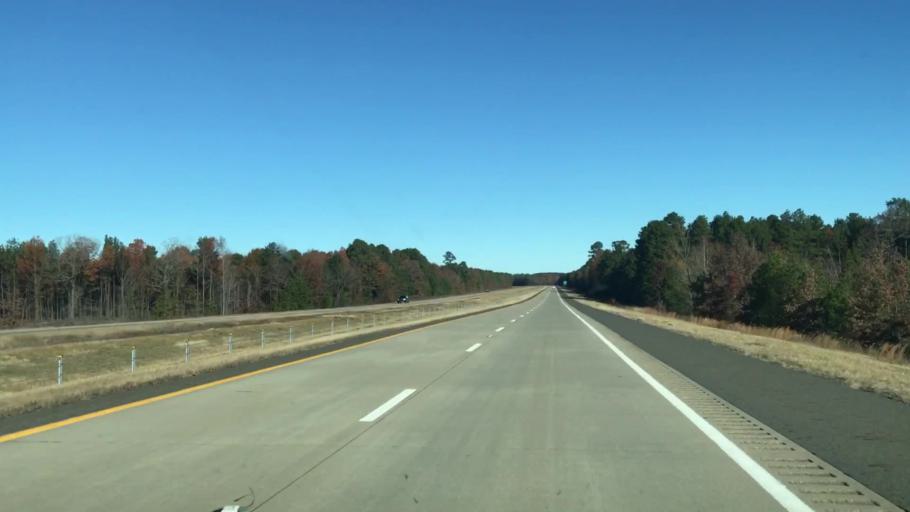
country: US
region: Texas
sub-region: Bowie County
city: Texarkana
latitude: 33.2268
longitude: -93.8732
